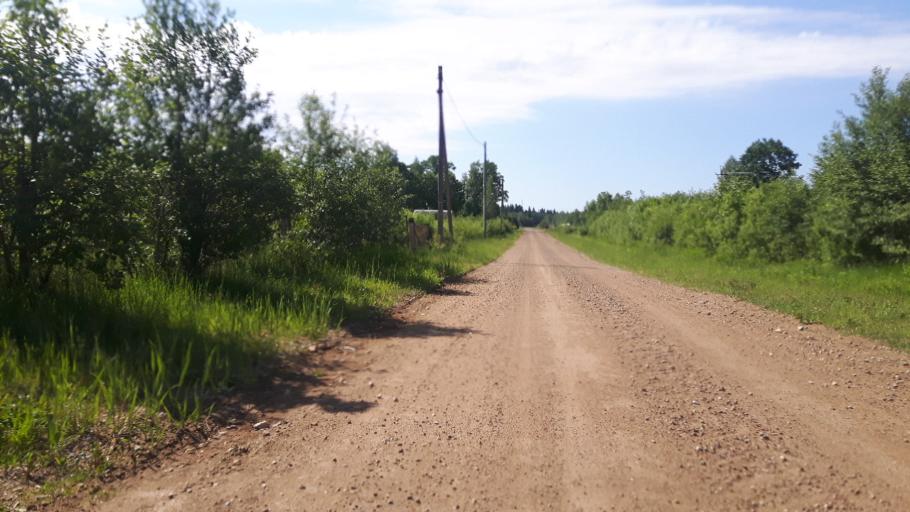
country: EE
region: Paernumaa
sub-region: Vaendra vald (alev)
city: Vandra
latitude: 58.6748
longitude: 25.0304
